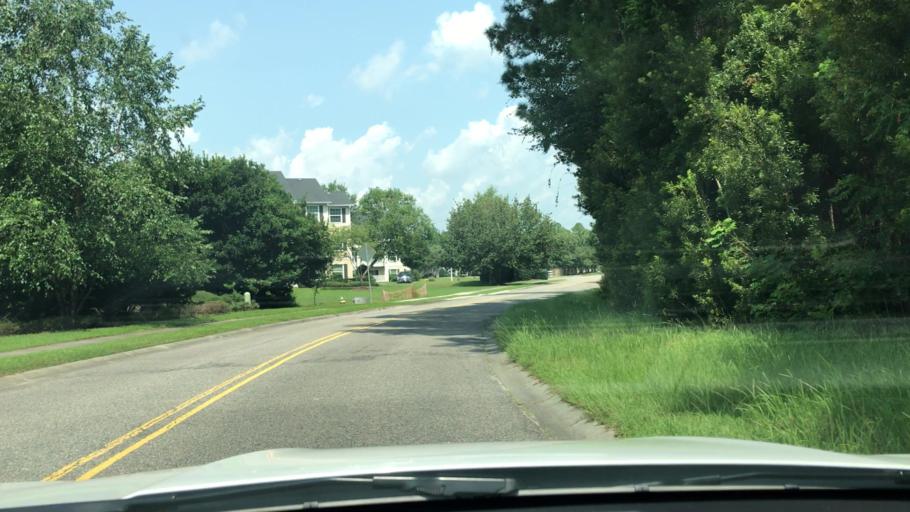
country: US
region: South Carolina
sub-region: Horry County
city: Forestbrook
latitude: 33.7790
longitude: -78.9648
